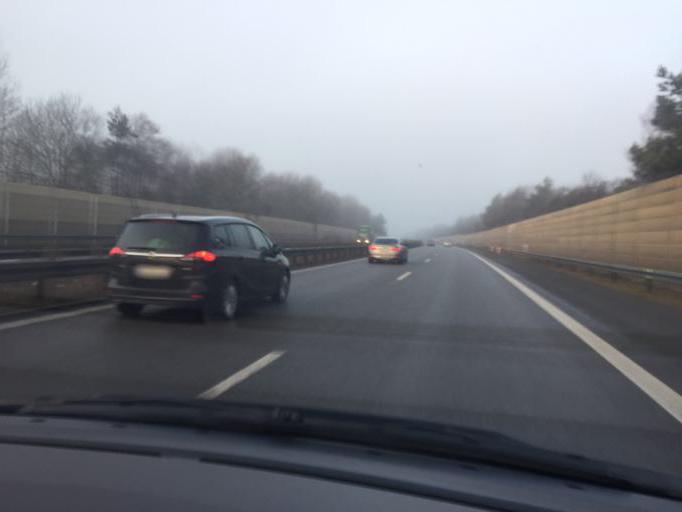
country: DE
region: Baden-Wuerttemberg
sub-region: Freiburg Region
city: Geisingen
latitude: 47.9252
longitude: 8.6611
